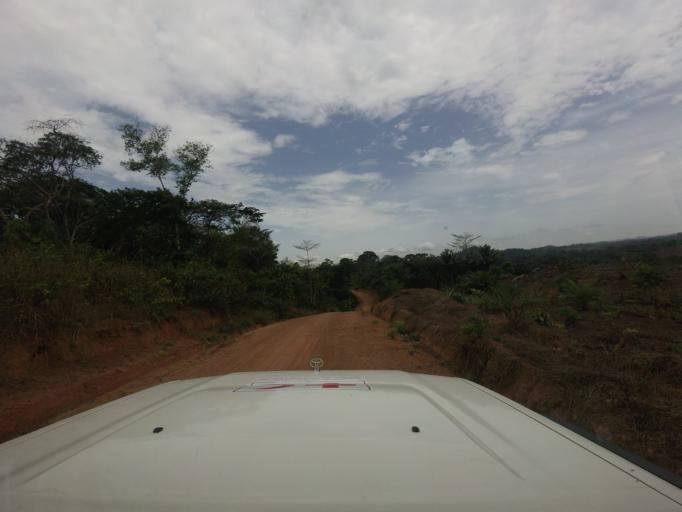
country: SL
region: Eastern Province
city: Buedu
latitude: 8.2615
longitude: -10.2338
